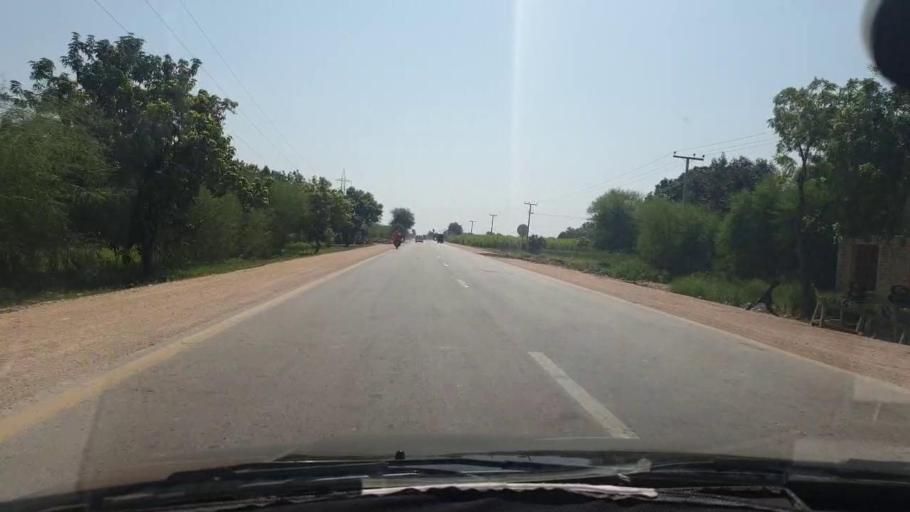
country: PK
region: Sindh
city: Chambar
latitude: 25.3640
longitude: 68.7847
